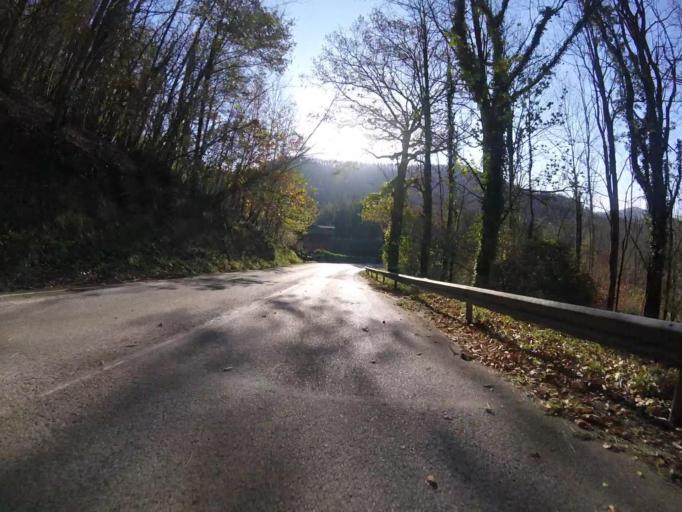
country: ES
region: Navarre
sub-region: Provincia de Navarra
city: Lesaka
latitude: 43.2398
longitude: -1.6722
